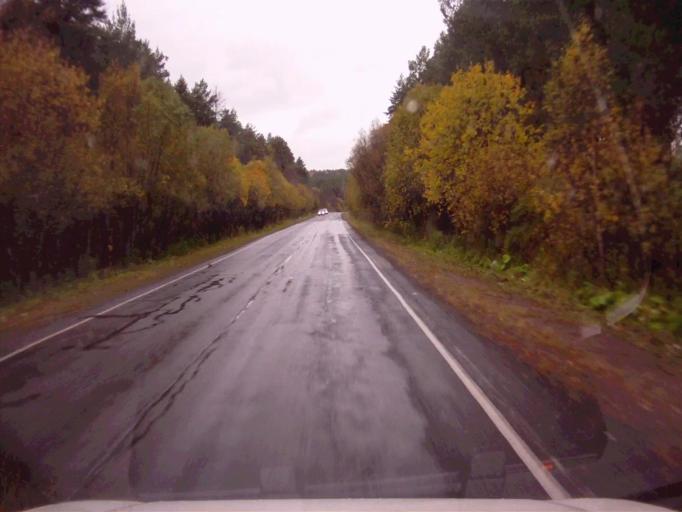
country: RU
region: Chelyabinsk
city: Verkhniy Ufaley
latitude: 56.0492
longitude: 60.1426
